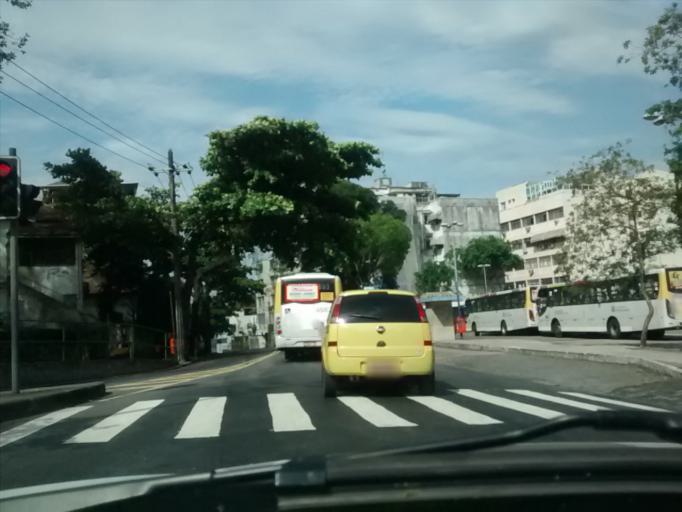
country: BR
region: Rio de Janeiro
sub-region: Rio De Janeiro
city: Rio de Janeiro
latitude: -22.9465
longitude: -43.2573
